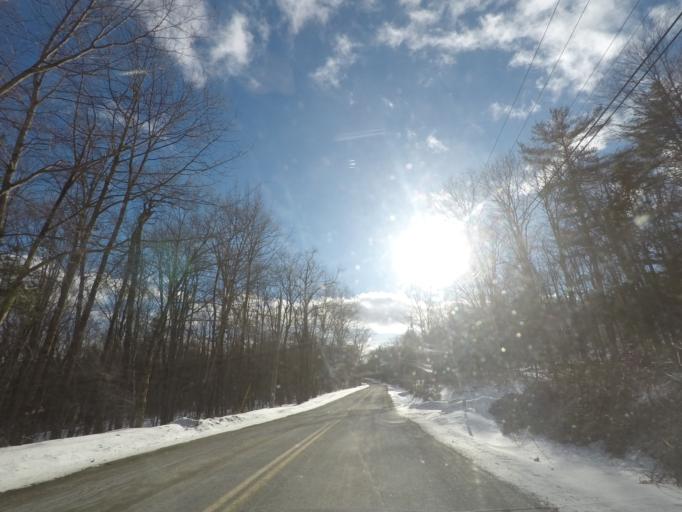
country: US
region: New York
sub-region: Rensselaer County
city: Hoosick Falls
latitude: 42.8092
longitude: -73.3931
